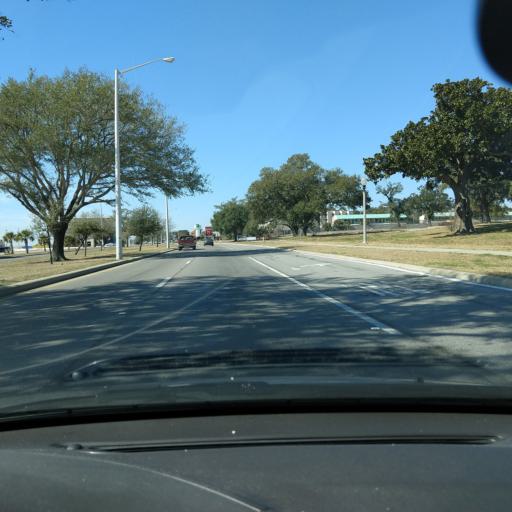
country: US
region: Mississippi
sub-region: Harrison County
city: Biloxi
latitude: 30.3936
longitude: -88.9350
